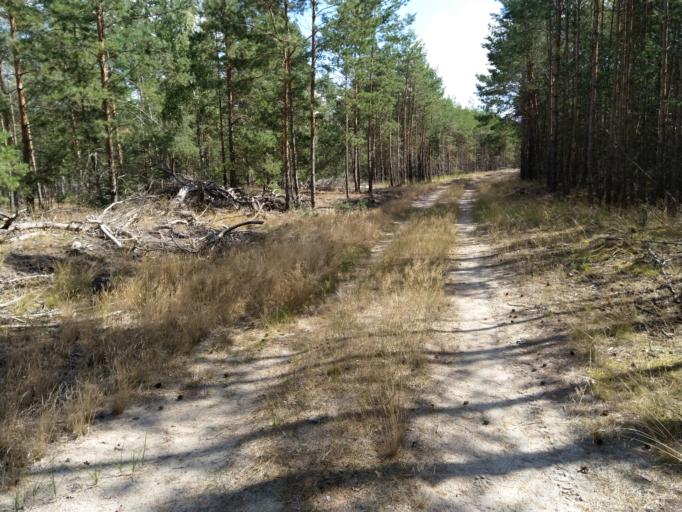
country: DE
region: Brandenburg
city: Luckenwalde
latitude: 52.0445
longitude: 13.1666
